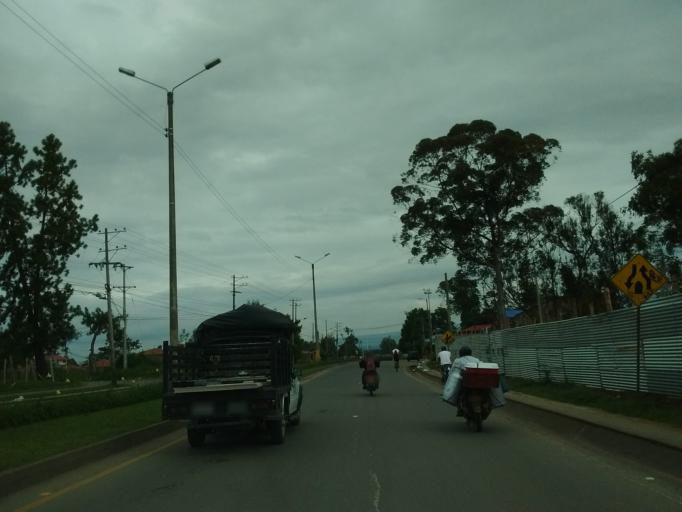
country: CO
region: Cauca
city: Popayan
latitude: 2.4901
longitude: -76.5597
